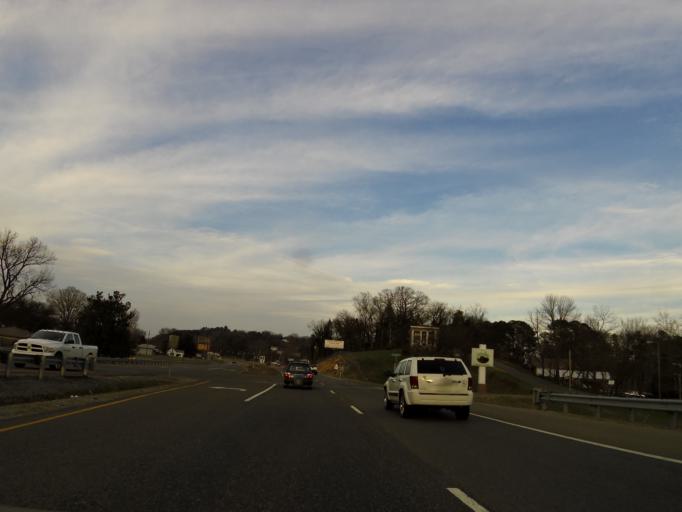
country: US
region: Tennessee
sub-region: Rhea County
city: Dayton
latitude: 35.4902
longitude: -85.0107
